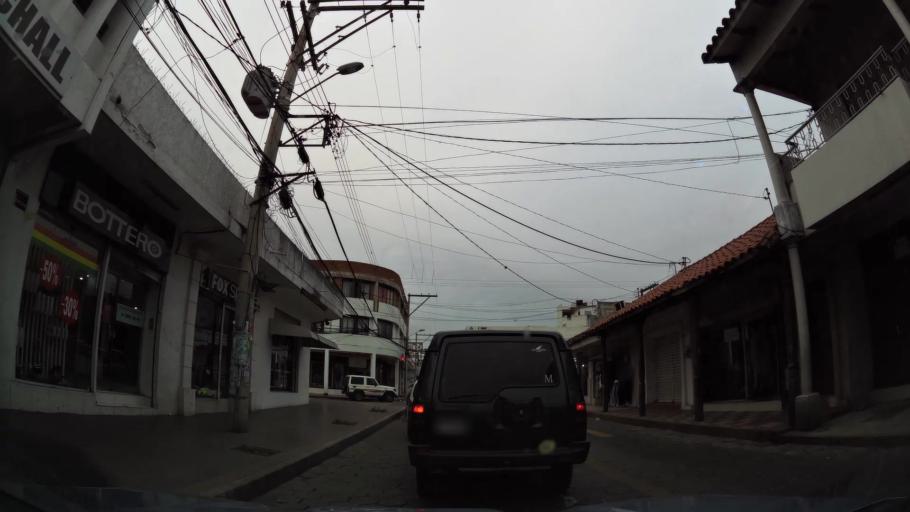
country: BO
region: Santa Cruz
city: Santa Cruz de la Sierra
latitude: -17.7871
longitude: -63.1844
